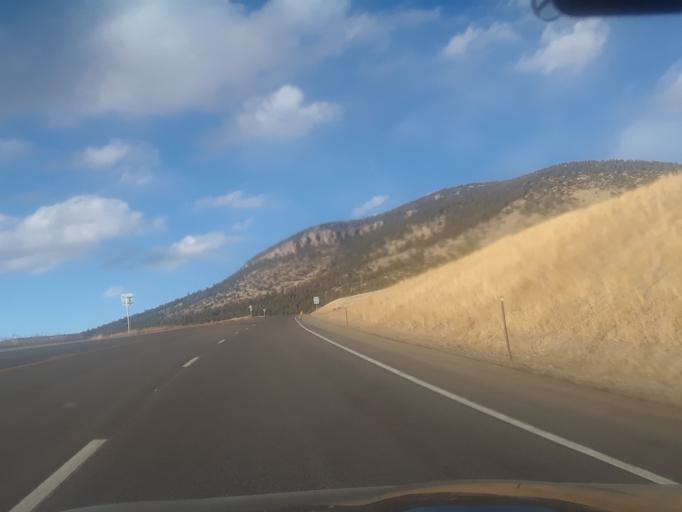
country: US
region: Colorado
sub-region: Chaffee County
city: Buena Vista
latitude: 38.8631
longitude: -105.9850
